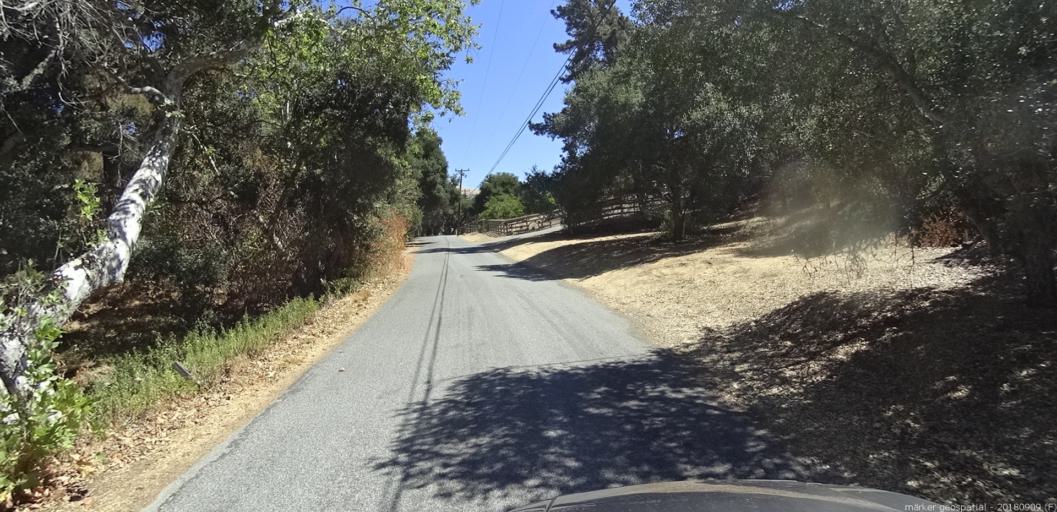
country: US
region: California
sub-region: Monterey County
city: Carmel Valley Village
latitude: 36.5670
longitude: -121.7013
